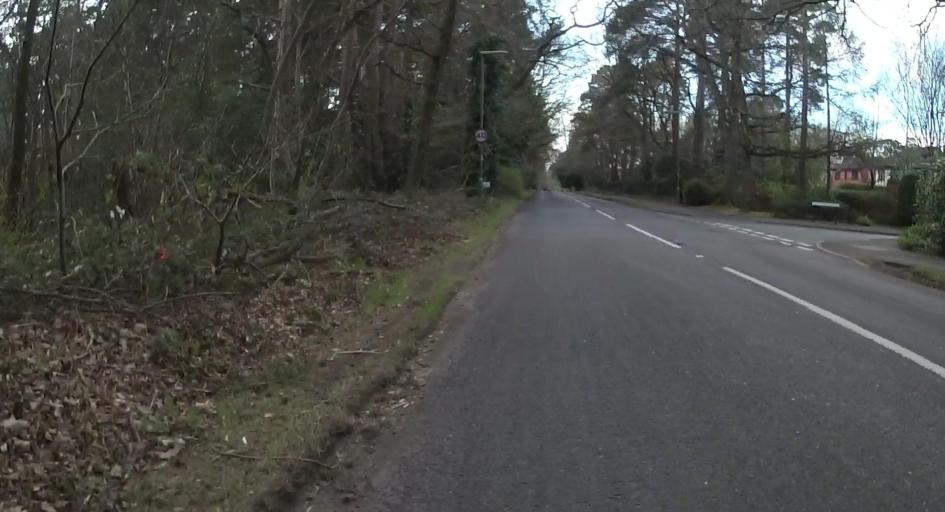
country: GB
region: England
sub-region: Surrey
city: Bagshot
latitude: 51.3224
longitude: -0.7006
